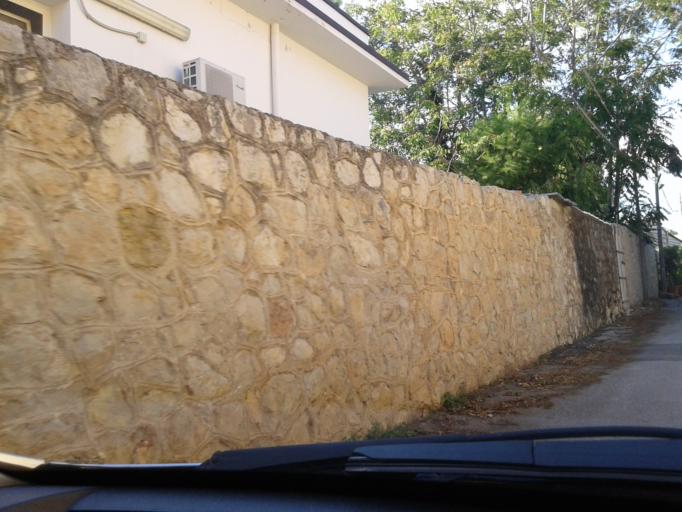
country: IT
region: Sicily
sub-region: Palermo
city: Palermo
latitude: 38.1040
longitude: 13.3152
